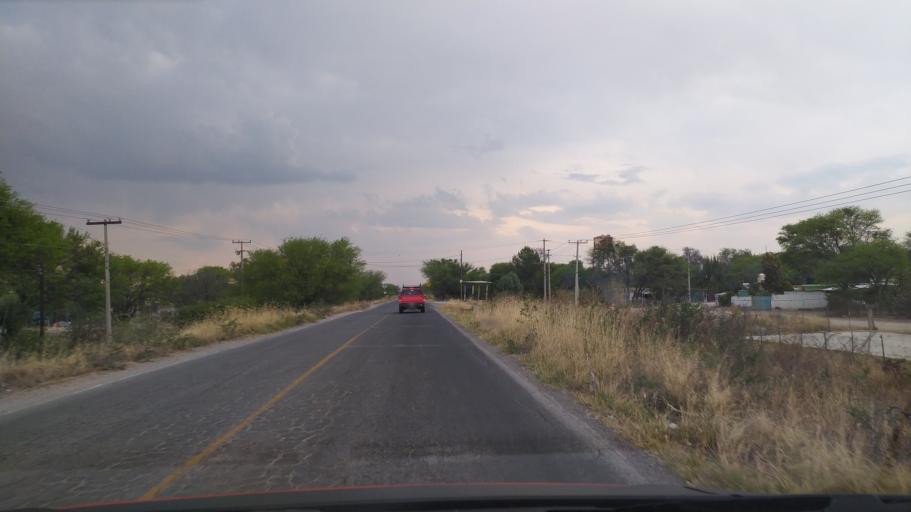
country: MX
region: Guanajuato
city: Ciudad Manuel Doblado
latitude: 20.8138
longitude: -101.9040
